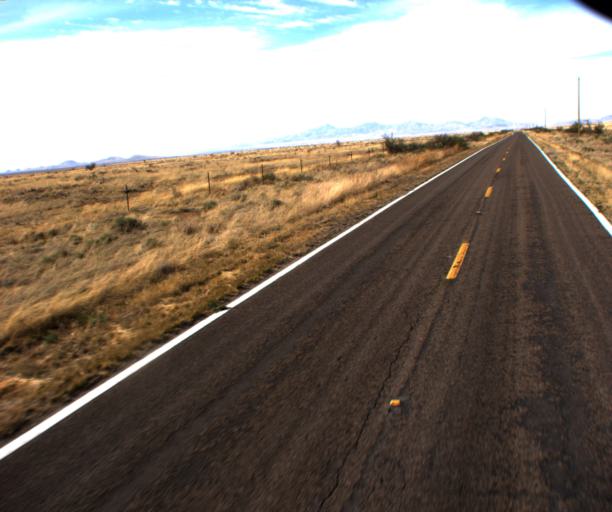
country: US
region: Arizona
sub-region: Cochise County
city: Willcox
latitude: 31.8943
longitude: -109.4913
